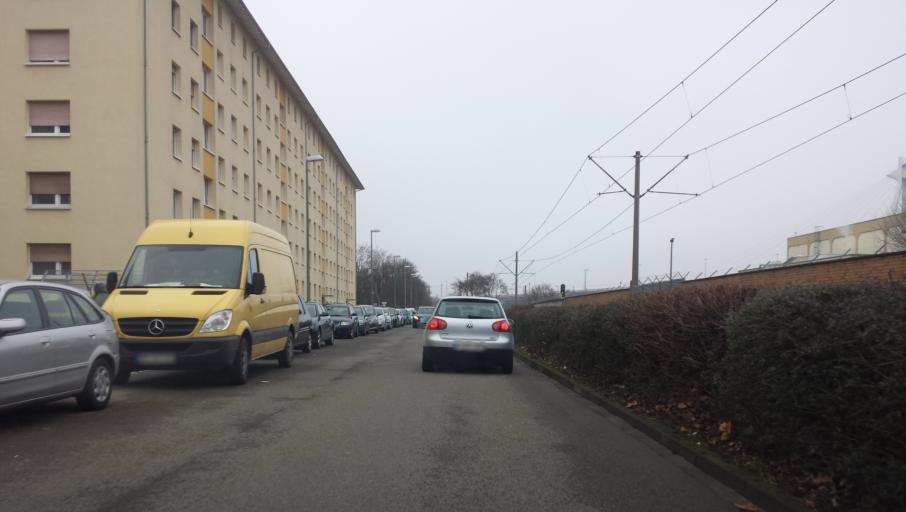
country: DE
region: Rheinland-Pfalz
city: Ludwigshafen am Rhein
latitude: 49.4740
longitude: 8.4356
